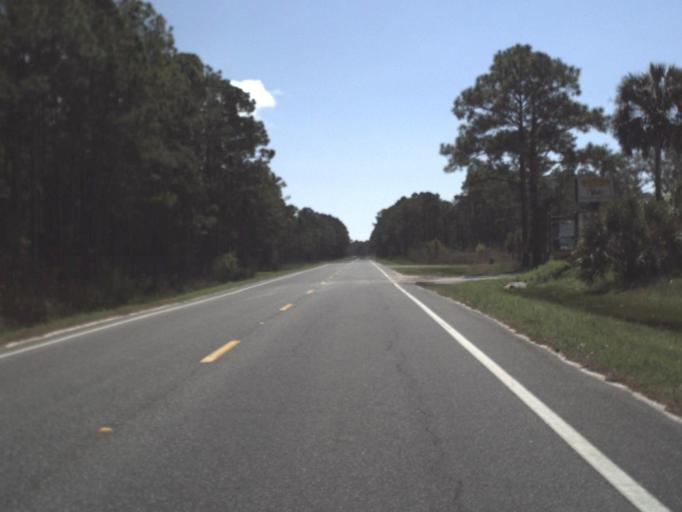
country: US
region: Florida
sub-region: Wakulla County
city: Crawfordville
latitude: 30.0105
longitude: -84.3947
